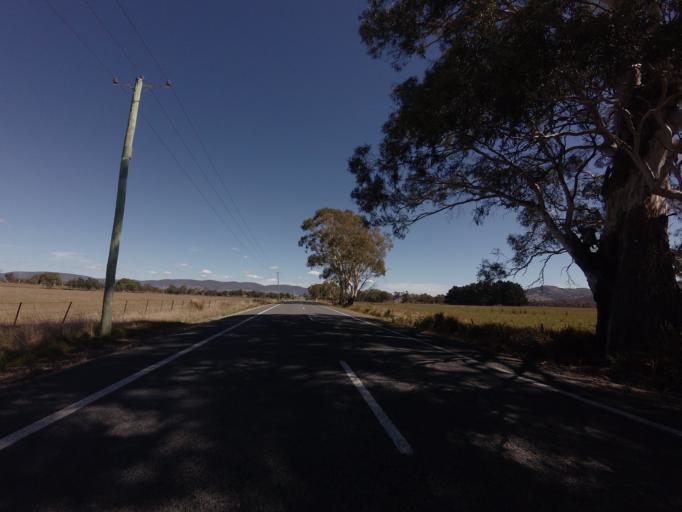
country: AU
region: Tasmania
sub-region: Northern Midlands
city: Evandale
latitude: -41.7646
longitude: 147.7464
